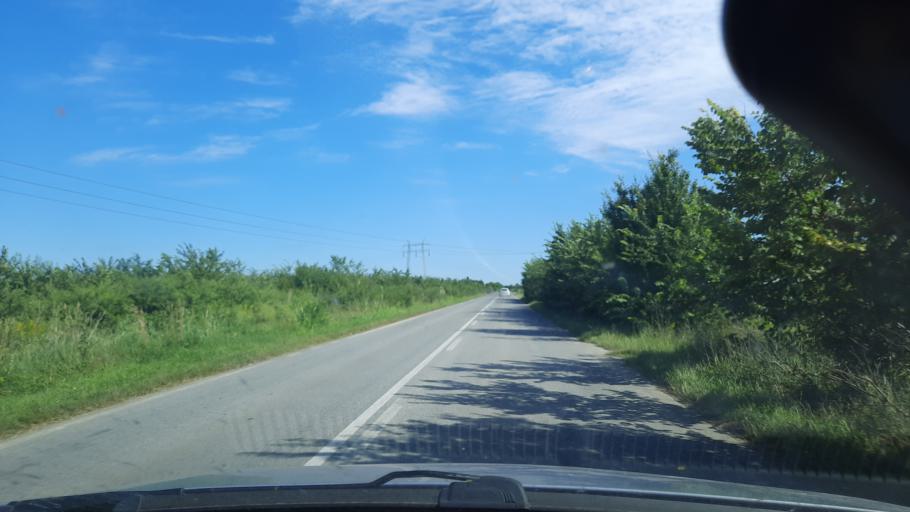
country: RS
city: Simanovci
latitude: 44.8515
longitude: 20.1004
